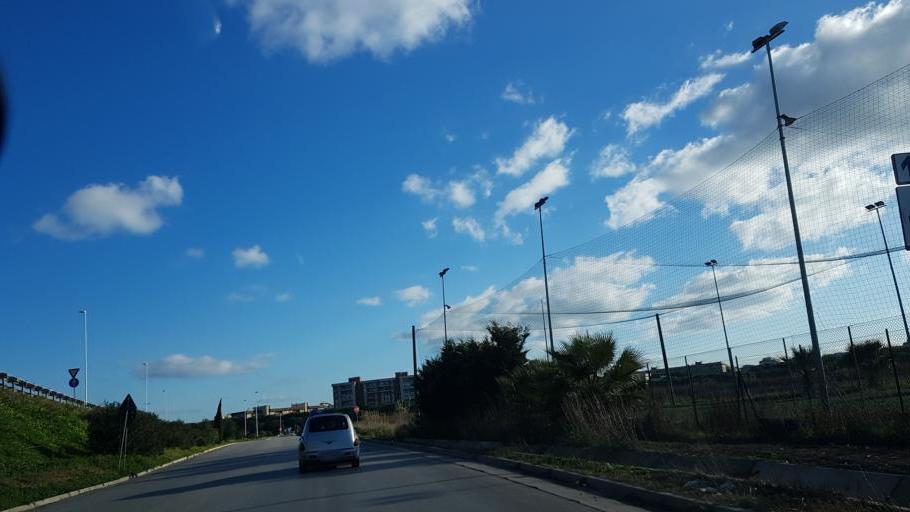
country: IT
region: Apulia
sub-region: Provincia di Brindisi
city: Brindisi
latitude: 40.6251
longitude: 17.9202
